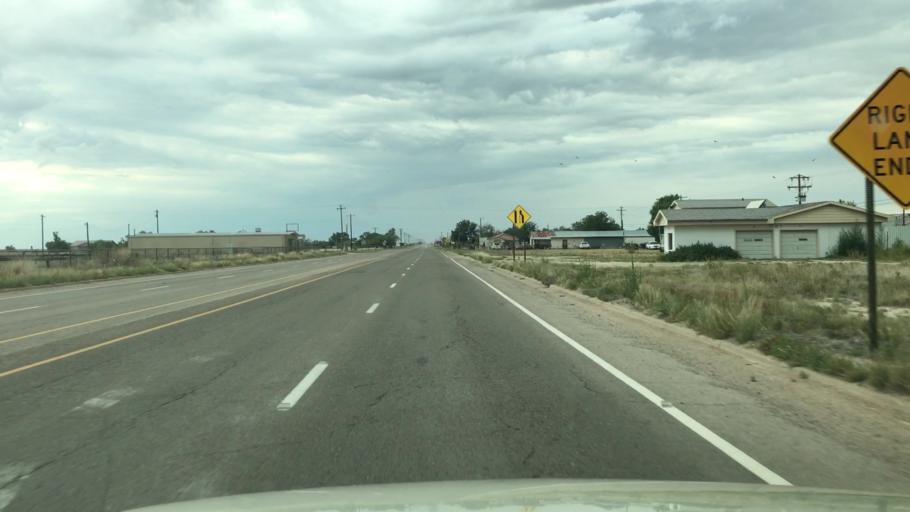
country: US
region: New Mexico
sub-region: Lea County
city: Lovington
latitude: 33.2570
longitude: -103.3327
